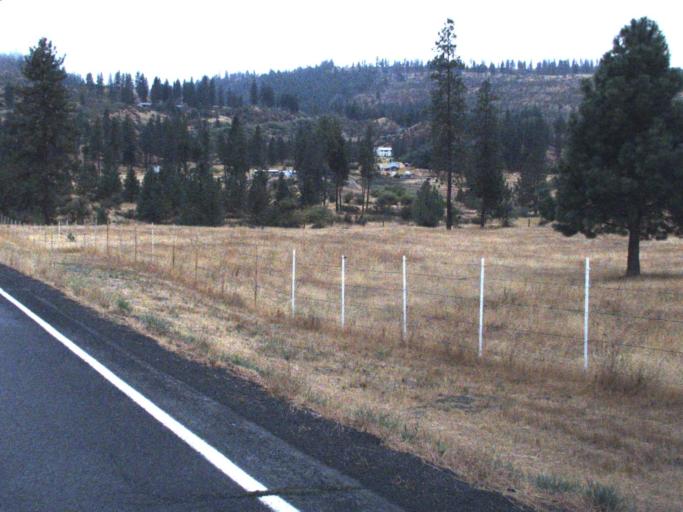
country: US
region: Washington
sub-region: Lincoln County
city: Davenport
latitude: 47.7842
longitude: -117.8891
